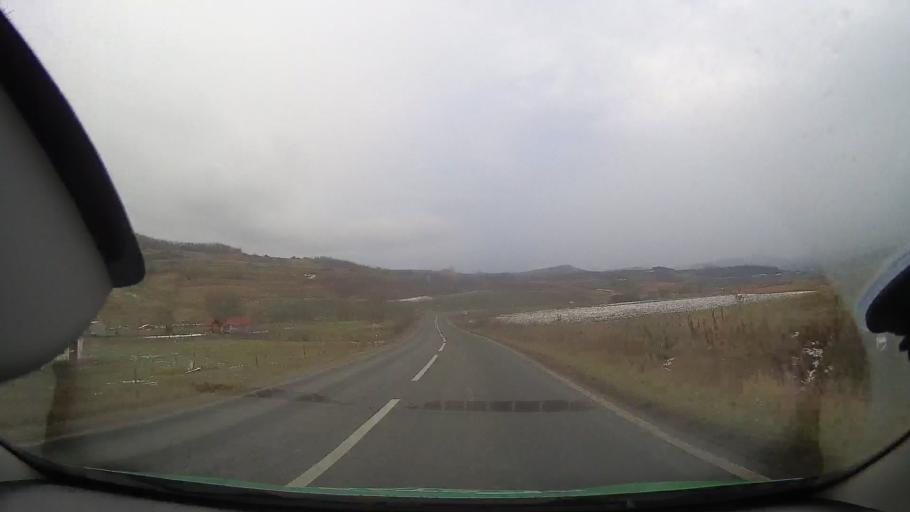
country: RO
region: Sibiu
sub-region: Comuna Blajel
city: Blajel
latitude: 46.2362
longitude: 24.3066
